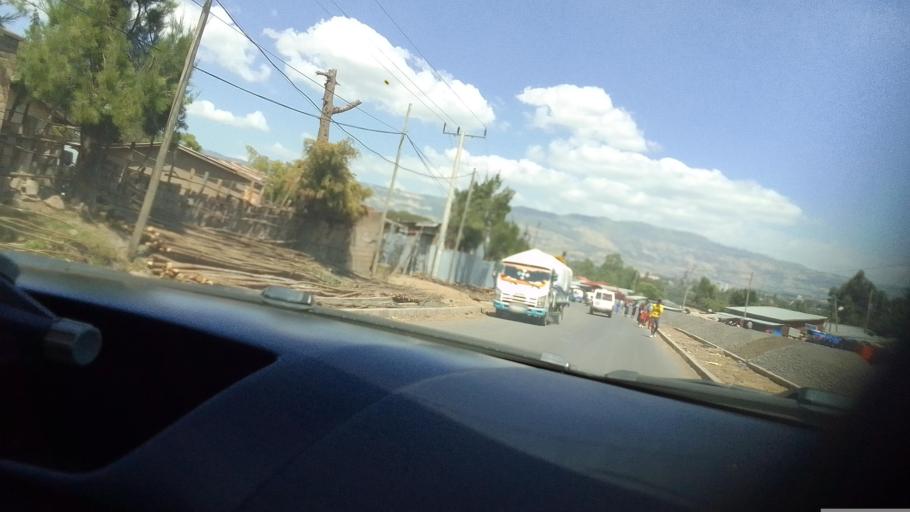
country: ET
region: Oromiya
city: Hagere Hiywet
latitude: 8.9724
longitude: 37.8513
